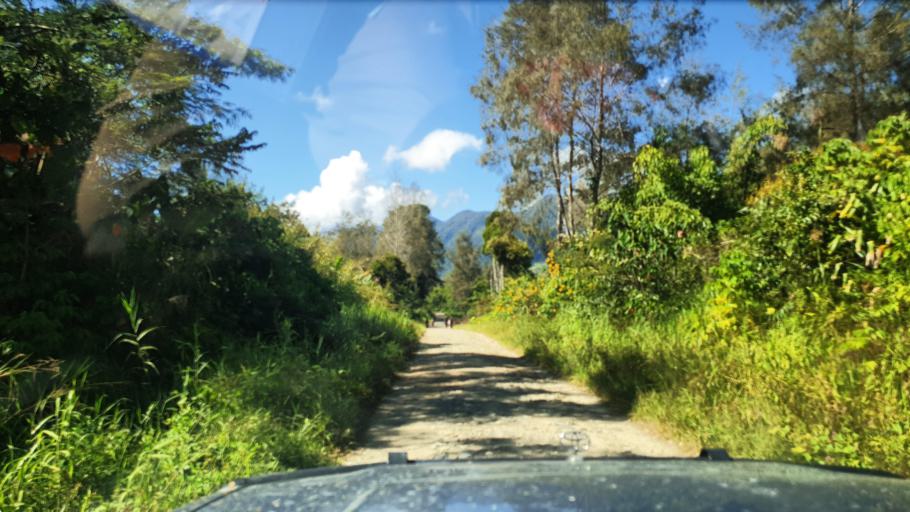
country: PG
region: Western Highlands
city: Rauna
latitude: -5.8138
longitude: 144.3789
